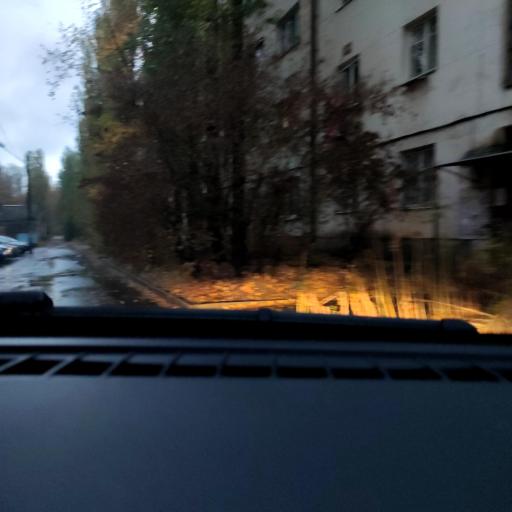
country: RU
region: Voronezj
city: Voronezh
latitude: 51.6905
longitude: 39.2650
